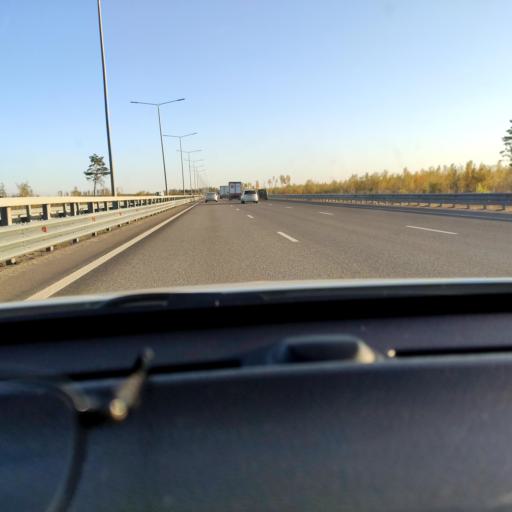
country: RU
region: Voronezj
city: Somovo
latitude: 51.7723
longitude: 39.3017
